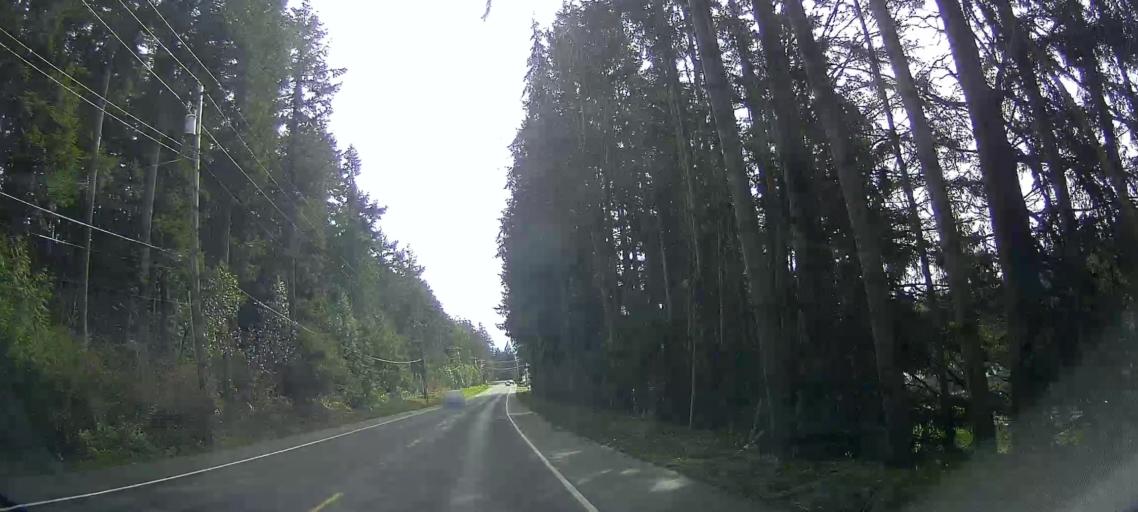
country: US
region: Washington
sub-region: Island County
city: Camano
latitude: 48.1412
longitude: -122.4683
